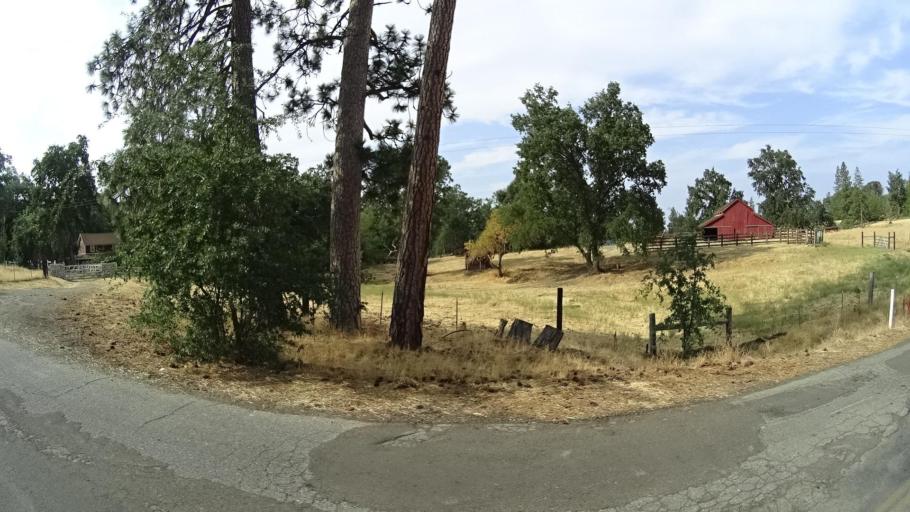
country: US
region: California
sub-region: Mariposa County
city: Midpines
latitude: 37.5005
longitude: -119.8086
